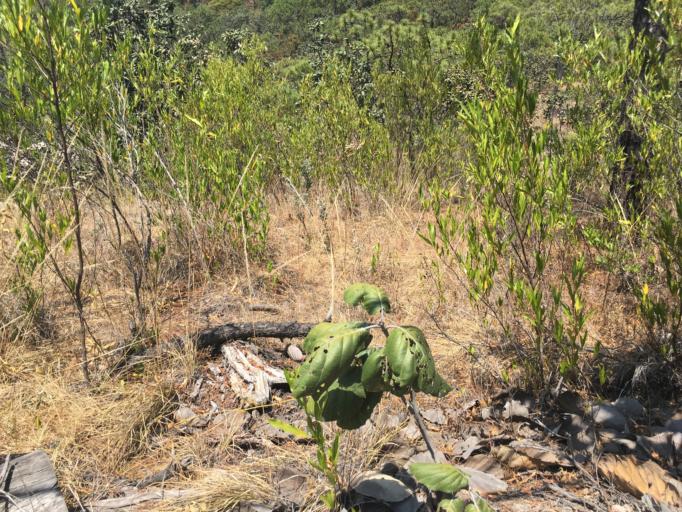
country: MX
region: Guerrero
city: Taxco de Alarcon
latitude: 18.5830
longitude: -99.6056
